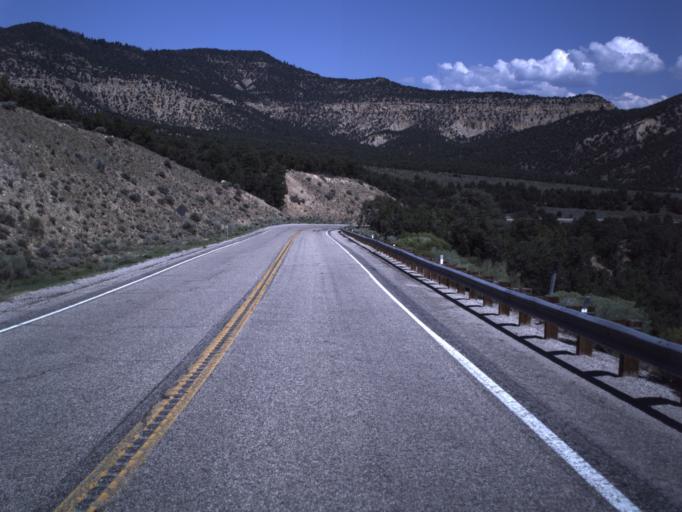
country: US
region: Utah
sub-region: Wayne County
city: Loa
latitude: 38.7235
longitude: -111.3989
